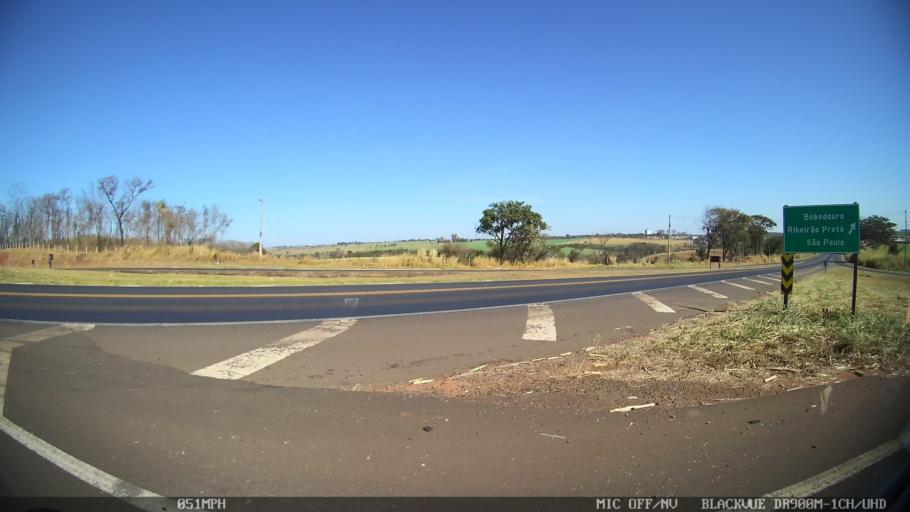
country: BR
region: Sao Paulo
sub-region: Olimpia
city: Olimpia
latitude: -20.6846
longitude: -48.9057
